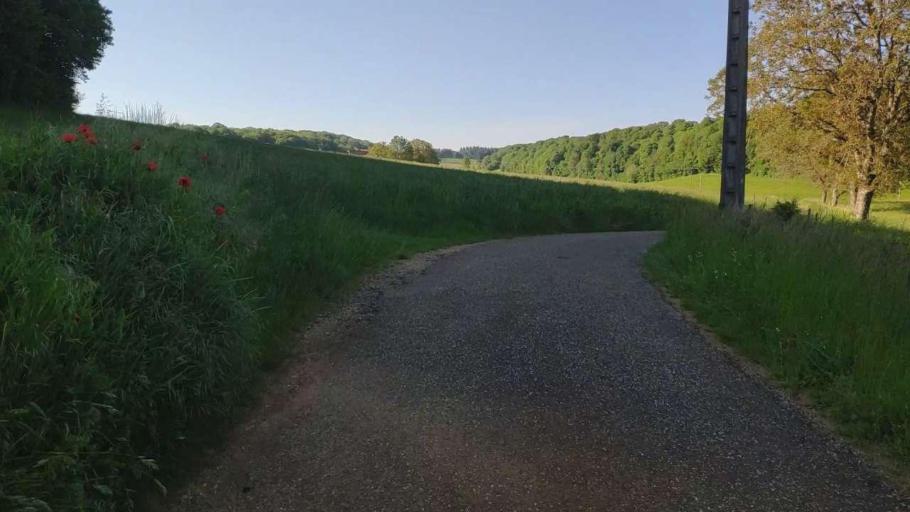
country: FR
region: Franche-Comte
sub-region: Departement du Jura
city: Perrigny
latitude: 46.7202
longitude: 5.6148
